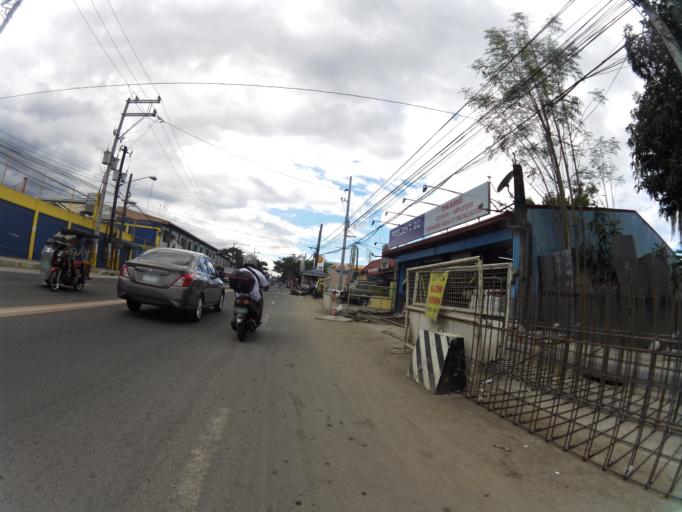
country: PH
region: Calabarzon
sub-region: Province of Rizal
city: Antipolo
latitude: 14.6331
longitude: 121.1112
